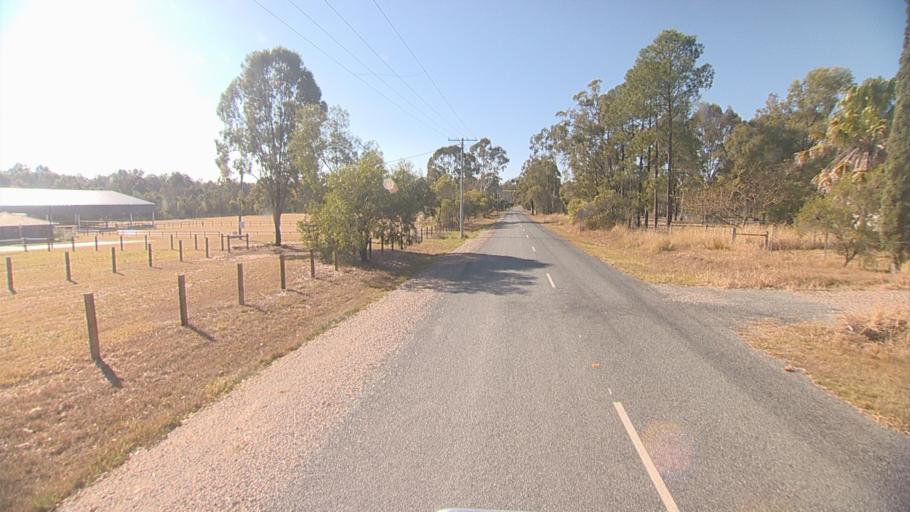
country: AU
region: Queensland
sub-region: Logan
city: Cedar Vale
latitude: -27.8410
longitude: 153.0275
